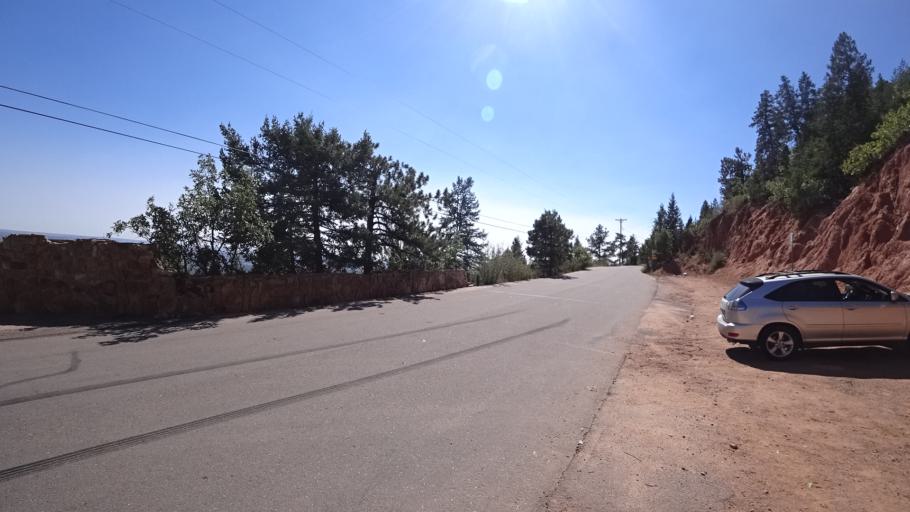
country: US
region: Colorado
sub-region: El Paso County
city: Colorado Springs
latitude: 38.8057
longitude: -104.8780
